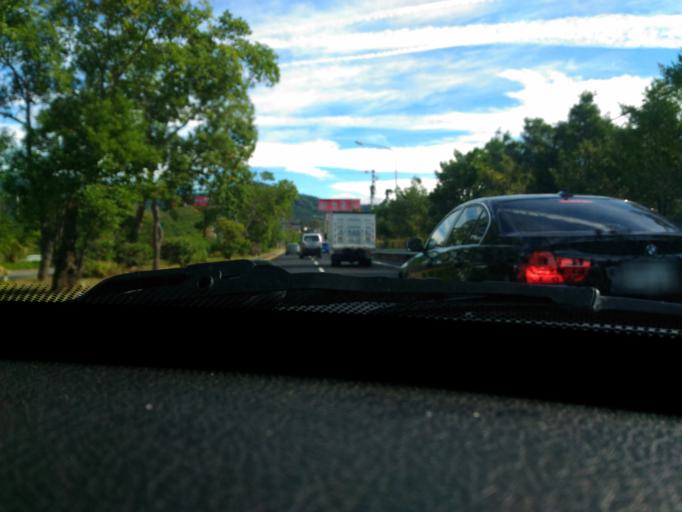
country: TW
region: Taiwan
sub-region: Hsinchu
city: Zhubei
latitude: 24.7650
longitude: 121.0839
